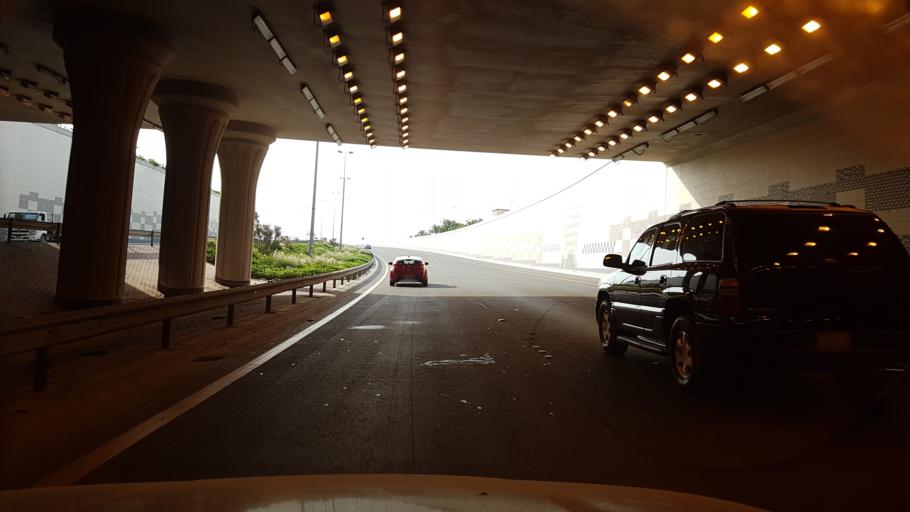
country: BH
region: Central Governorate
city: Madinat Hamad
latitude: 26.0978
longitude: 50.5114
